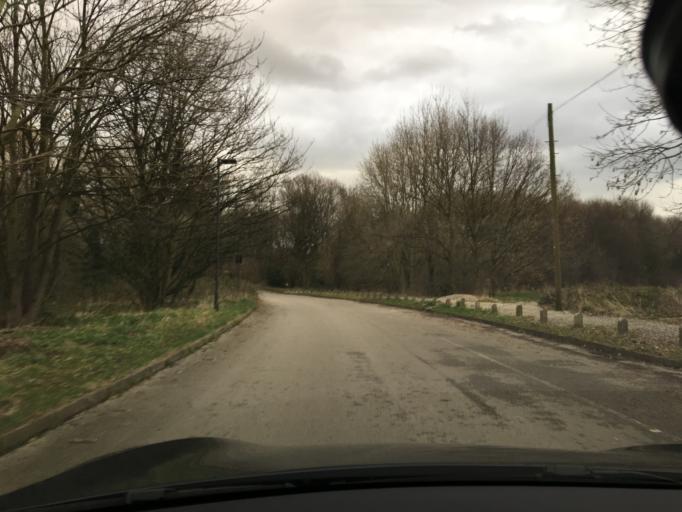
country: GB
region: England
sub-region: Manchester
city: Chorlton cum Hardy
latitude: 53.4382
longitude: -2.2525
